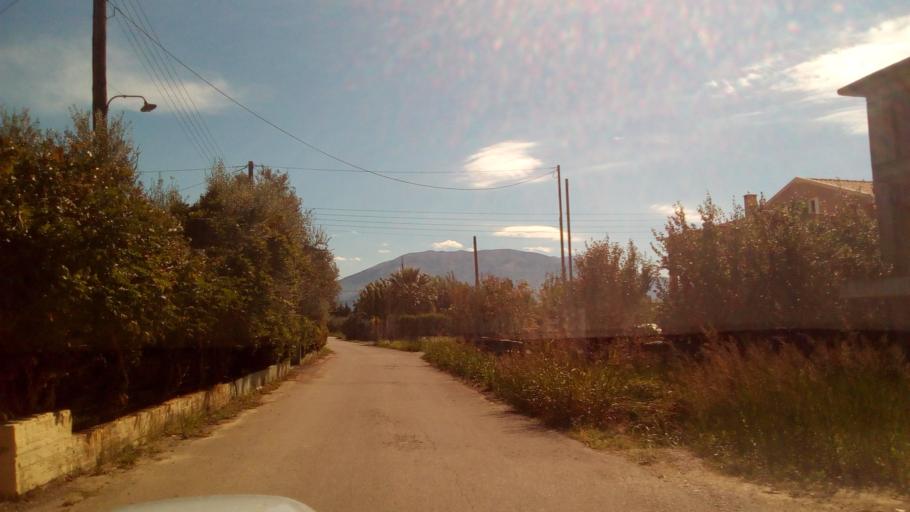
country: GR
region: West Greece
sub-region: Nomos Aitolias kai Akarnanias
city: Nafpaktos
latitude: 38.3796
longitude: 21.8014
